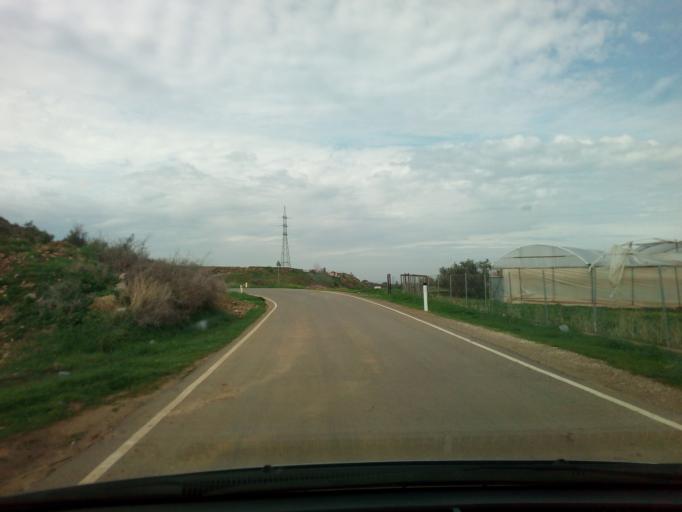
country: CY
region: Lefkosia
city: Astromeritis
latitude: 35.0954
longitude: 32.9897
